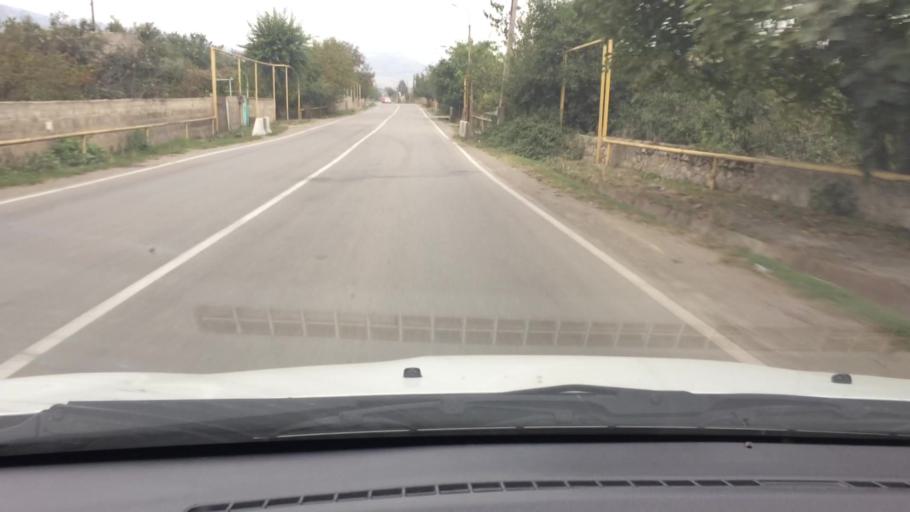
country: AM
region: Tavush
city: Bagratashen
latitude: 41.2390
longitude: 44.8023
